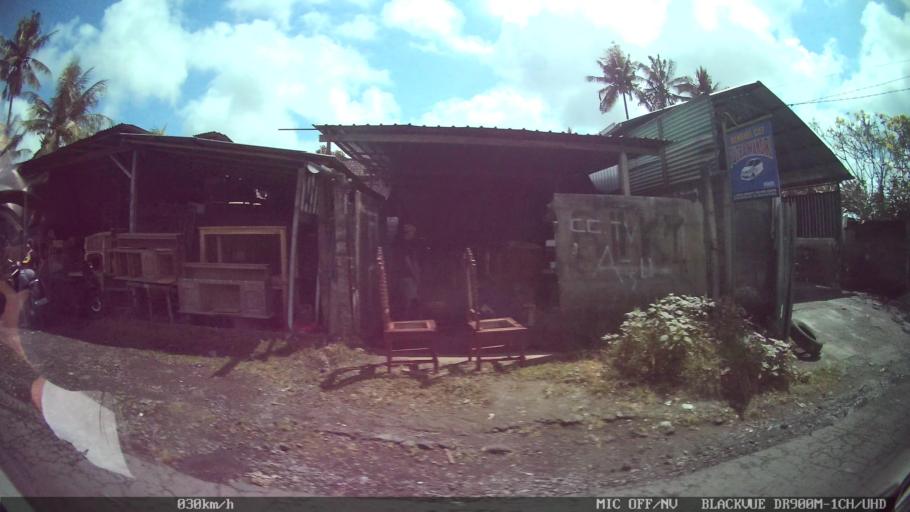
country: ID
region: Bali
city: Banjar Sedang
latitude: -8.5617
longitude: 115.2710
